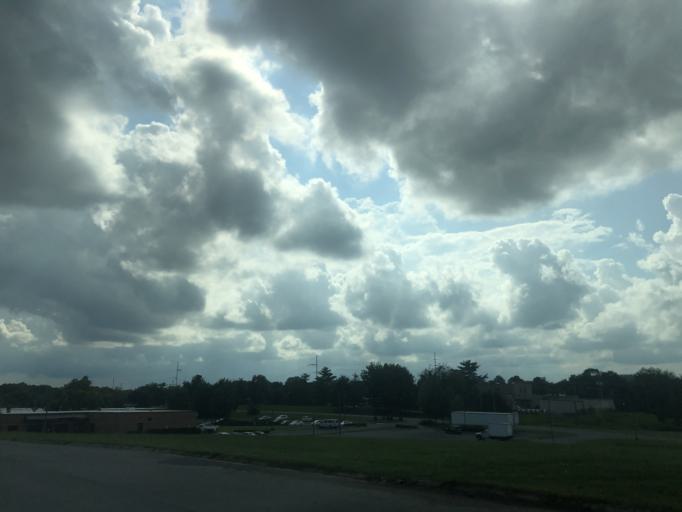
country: US
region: Tennessee
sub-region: Davidson County
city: Lakewood
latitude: 36.1661
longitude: -86.6448
